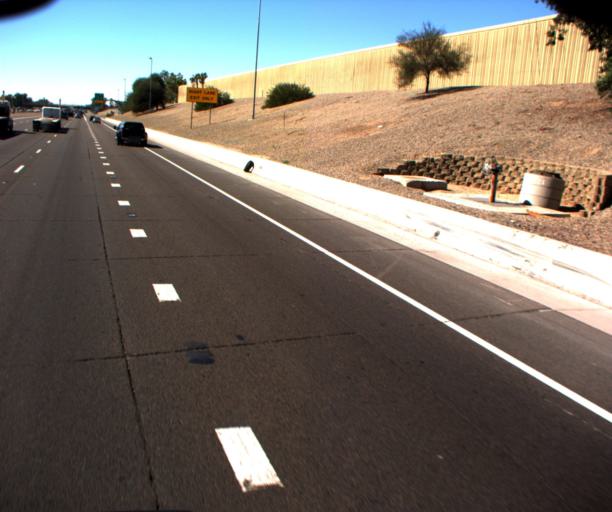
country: US
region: Arizona
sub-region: Maricopa County
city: Tolleson
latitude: 33.4629
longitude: -112.2117
